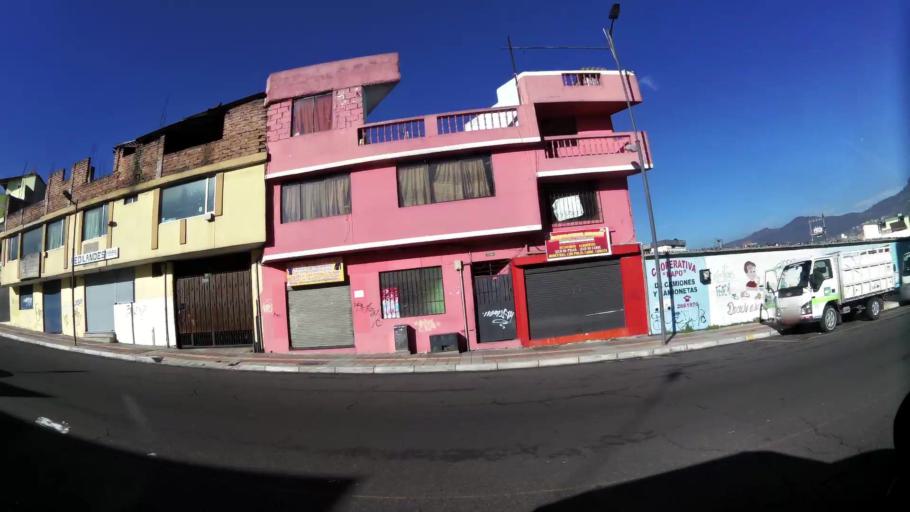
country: EC
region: Pichincha
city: Quito
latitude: -0.2450
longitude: -78.5173
